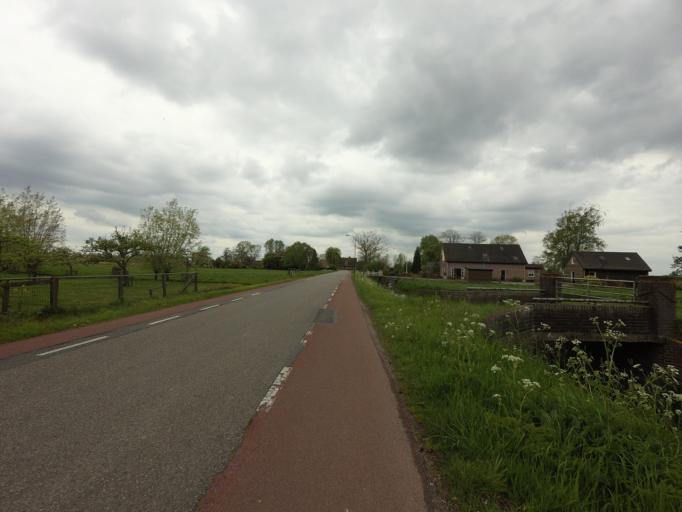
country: NL
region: North Holland
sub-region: Gemeente Wijdemeren
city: Nieuw-Loosdrecht
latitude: 52.1590
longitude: 5.1044
